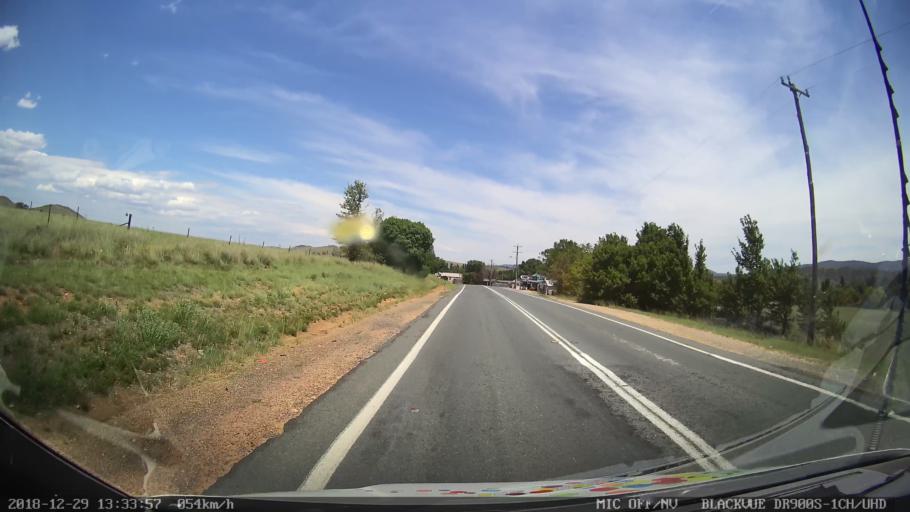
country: AU
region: New South Wales
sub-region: Cooma-Monaro
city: Cooma
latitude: -35.9496
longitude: 149.1458
